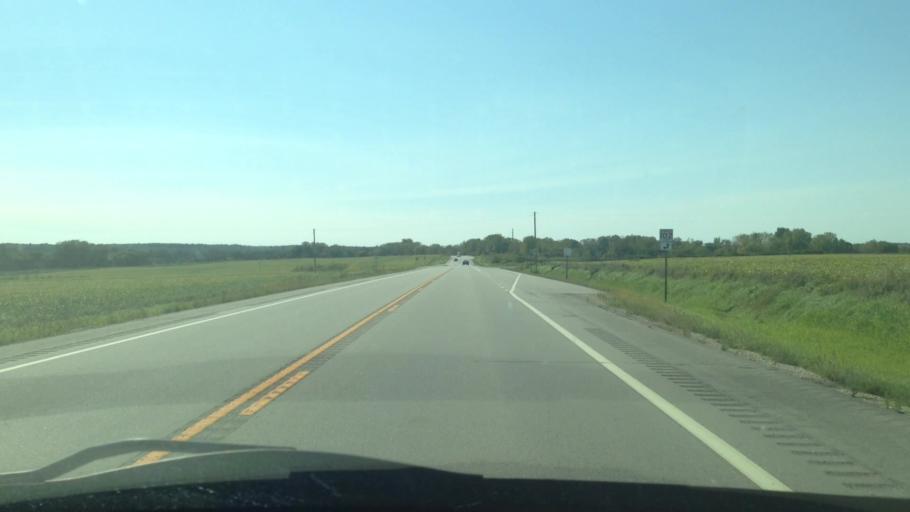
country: US
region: Minnesota
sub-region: Olmsted County
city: Eyota
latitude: 43.9994
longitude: -92.2769
